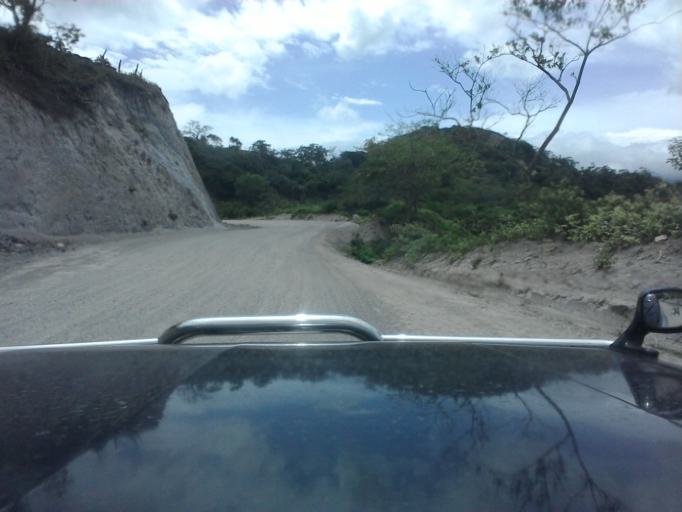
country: CR
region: Guanacaste
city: Juntas
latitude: 10.2377
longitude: -84.8538
